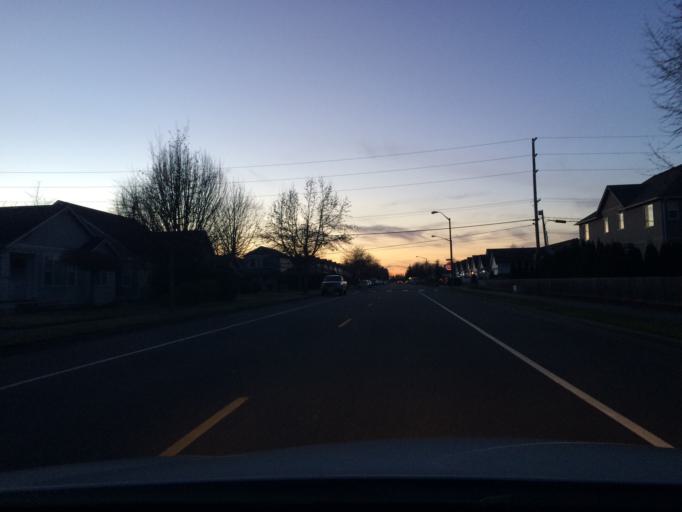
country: US
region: Washington
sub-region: Whatcom County
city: Lynden
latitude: 48.9624
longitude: -122.4286
